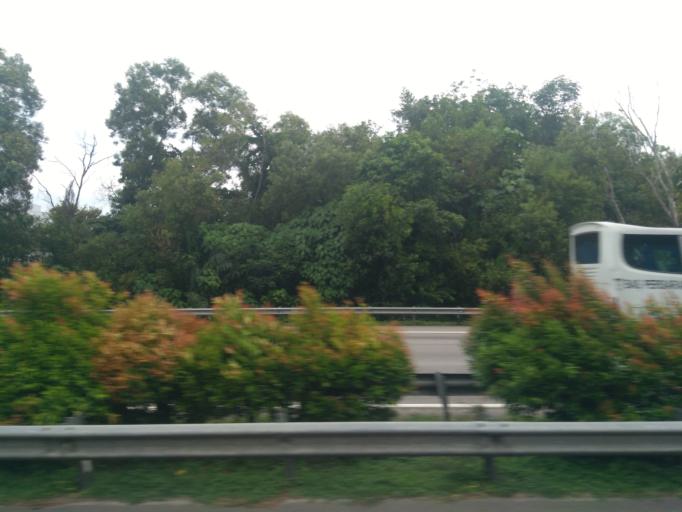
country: MY
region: Melaka
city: Pulau Sebang
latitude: 2.4269
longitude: 102.2103
